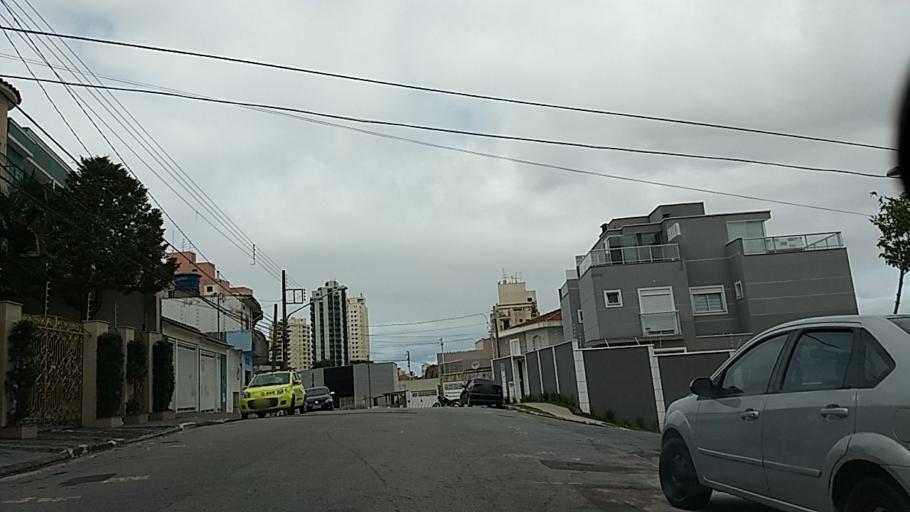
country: BR
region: Sao Paulo
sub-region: Sao Paulo
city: Sao Paulo
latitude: -23.5035
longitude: -46.6061
